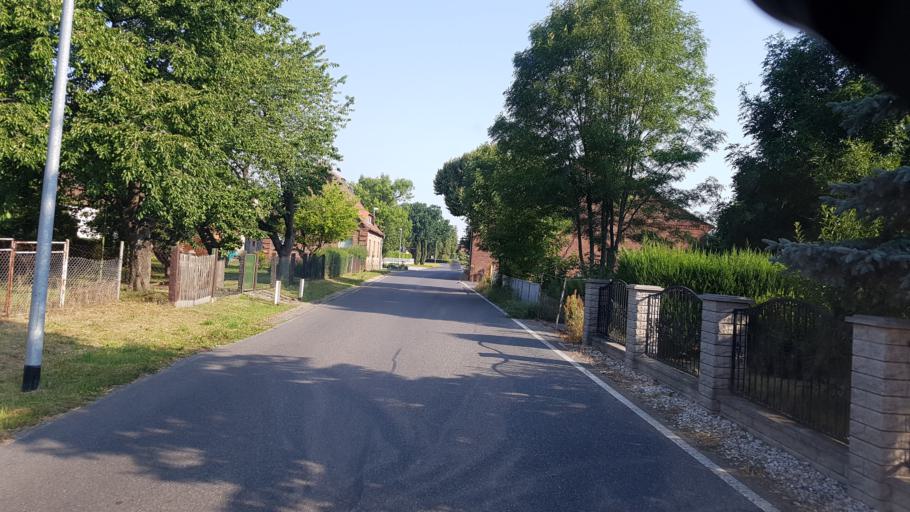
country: DE
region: Brandenburg
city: Drebkau
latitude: 51.6697
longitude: 14.2333
